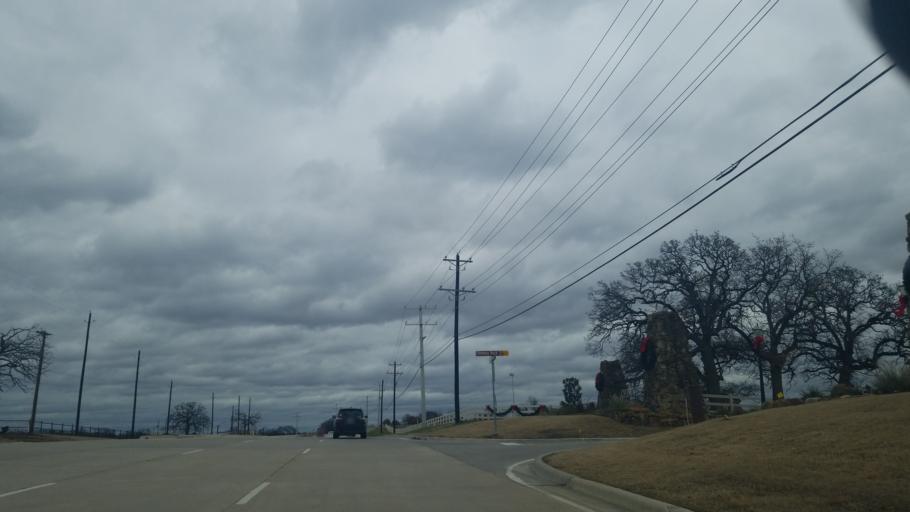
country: US
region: Texas
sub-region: Denton County
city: Bartonville
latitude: 33.0433
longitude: -97.1565
